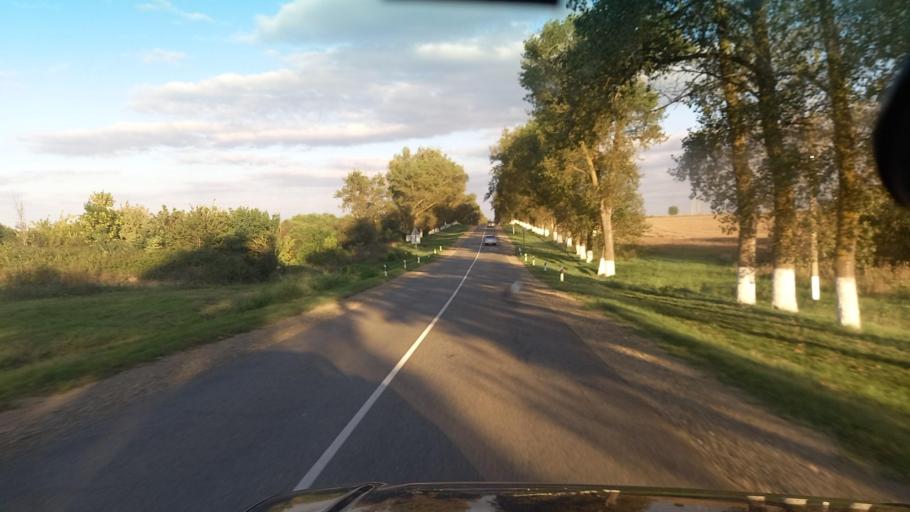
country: RU
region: Krasnodarskiy
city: Krymsk
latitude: 44.9400
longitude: 37.9288
